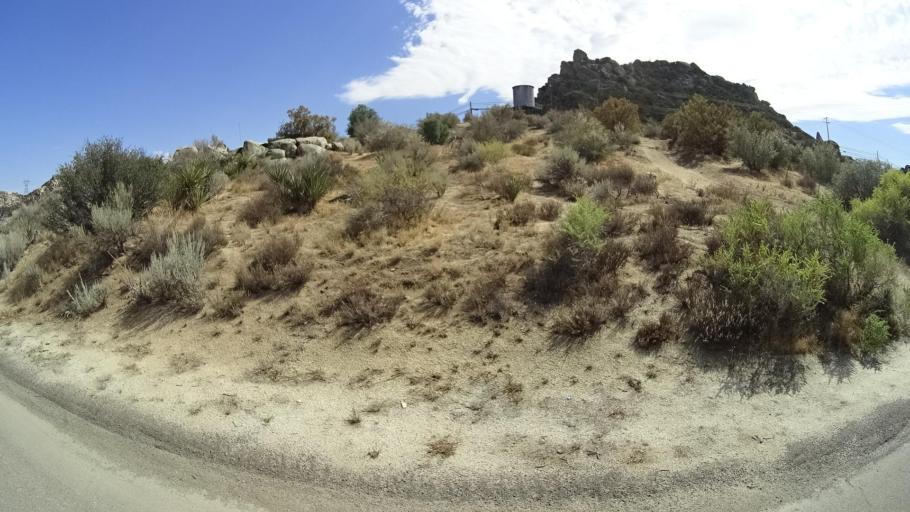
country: MX
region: Baja California
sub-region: Tecate
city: Cereso del Hongo
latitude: 32.6599
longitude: -116.2513
